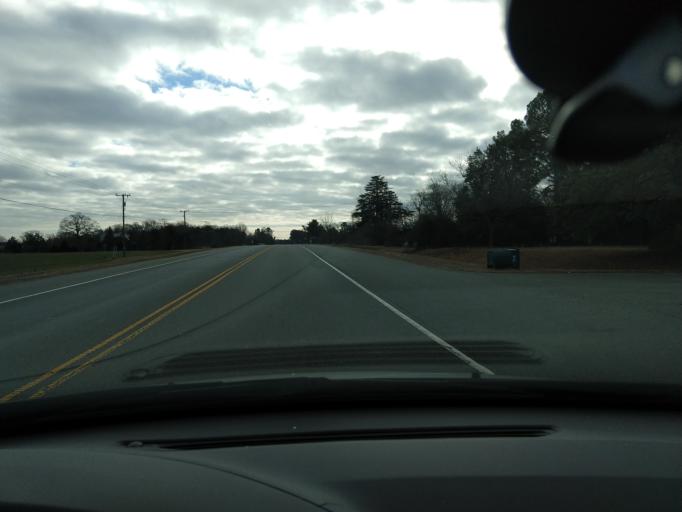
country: US
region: Virginia
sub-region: Henrico County
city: Fort Lee
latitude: 37.4631
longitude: -77.3806
